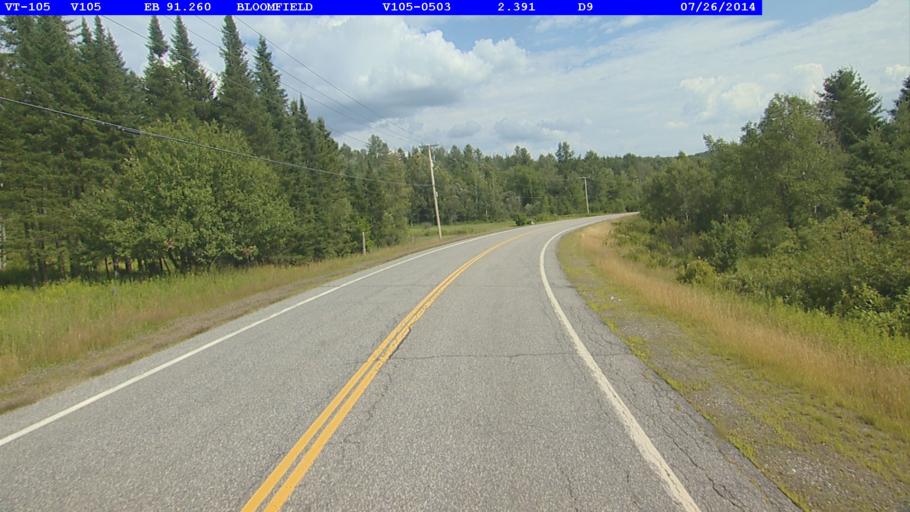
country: US
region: New Hampshire
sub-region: Coos County
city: Stratford
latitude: 44.7748
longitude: -71.6459
